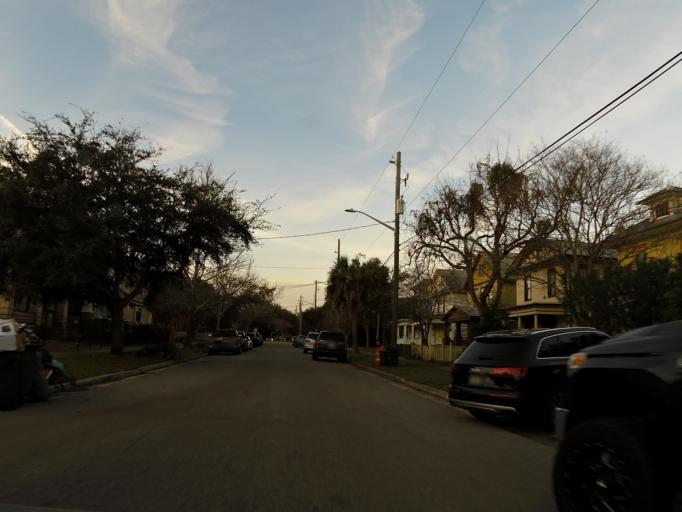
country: US
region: Florida
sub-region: Duval County
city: Jacksonville
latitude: 30.3450
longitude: -81.6572
